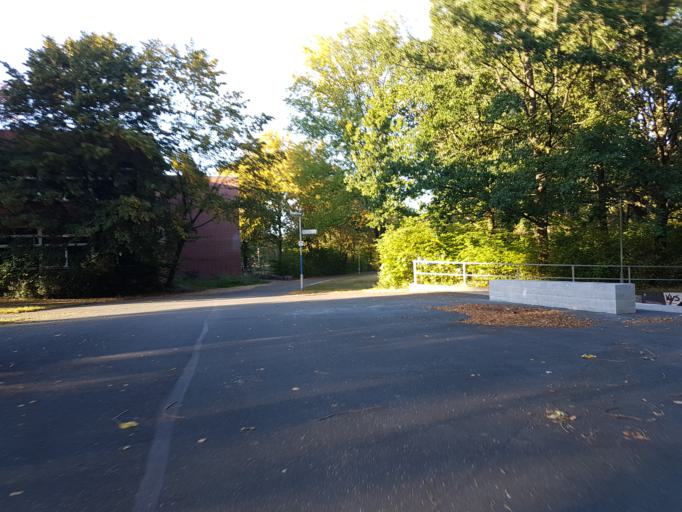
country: DE
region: Lower Saxony
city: Langenhagen
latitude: 52.4129
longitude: 9.7503
